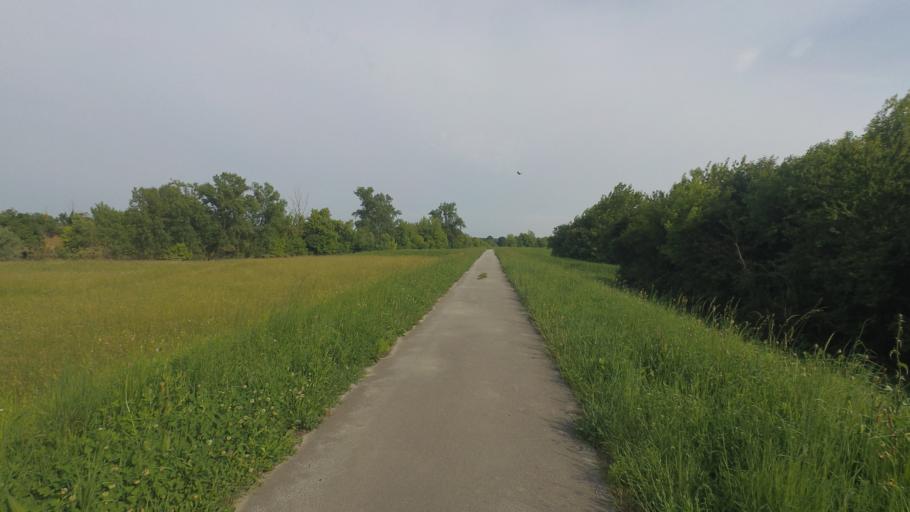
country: HR
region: Karlovacka
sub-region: Grad Karlovac
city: Karlovac
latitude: 45.4943
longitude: 15.5701
